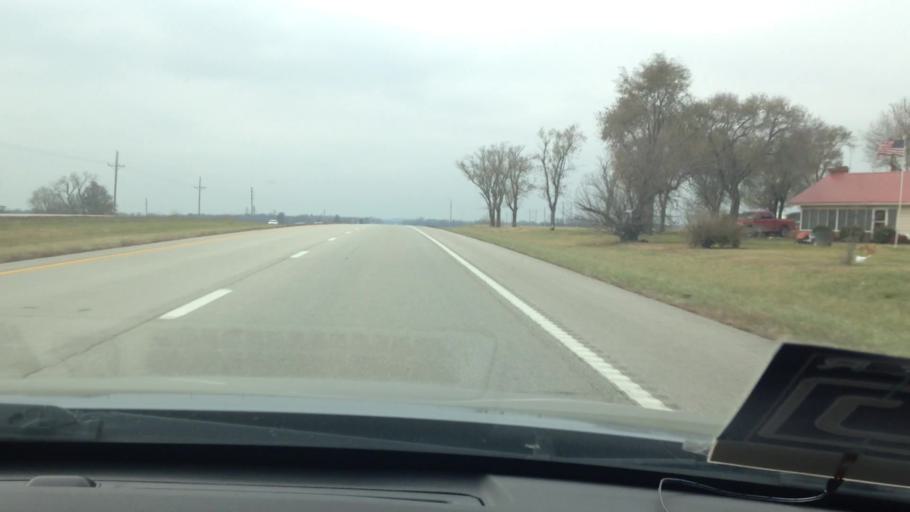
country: US
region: Missouri
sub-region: Cass County
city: Garden City
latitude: 38.5849
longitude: -94.2262
